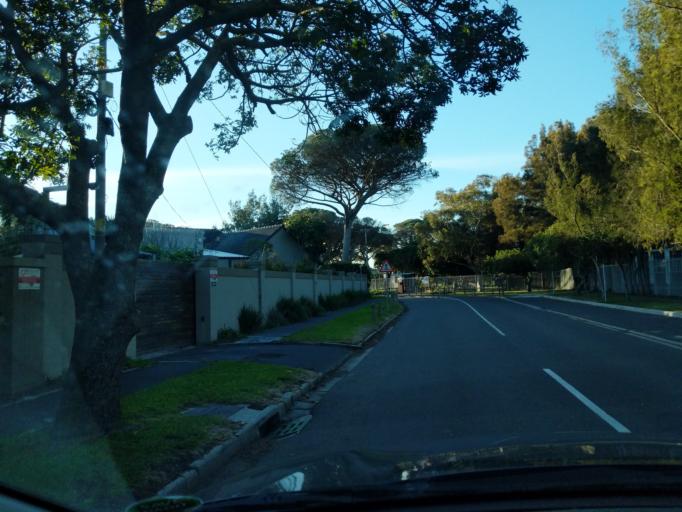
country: ZA
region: Western Cape
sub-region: City of Cape Town
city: Rosebank
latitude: -33.9373
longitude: 18.5064
